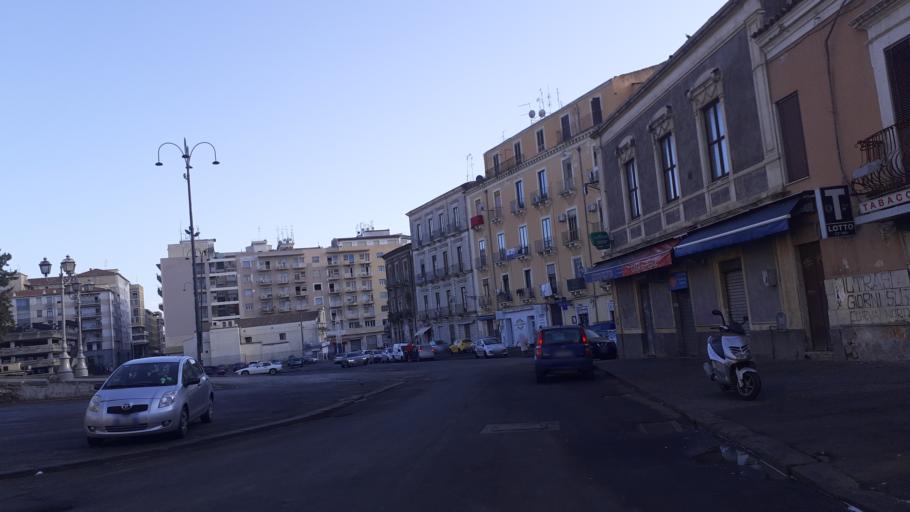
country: IT
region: Sicily
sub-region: Catania
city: Catania
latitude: 37.5103
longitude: 15.0882
